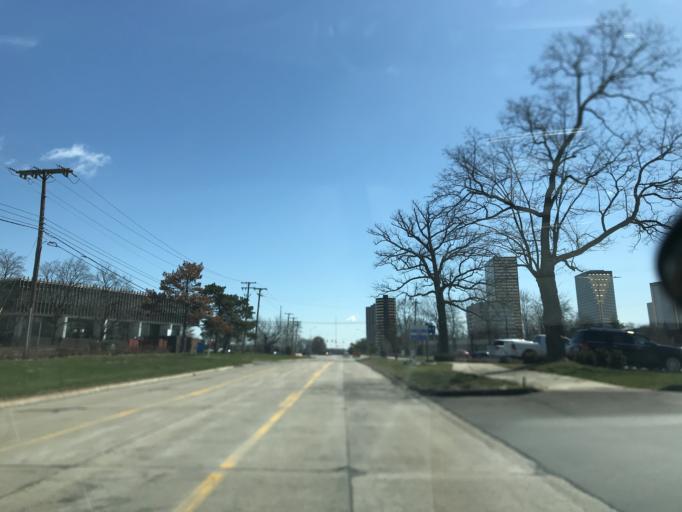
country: US
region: Michigan
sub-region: Oakland County
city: Southfield
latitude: 42.4792
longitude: -83.2554
